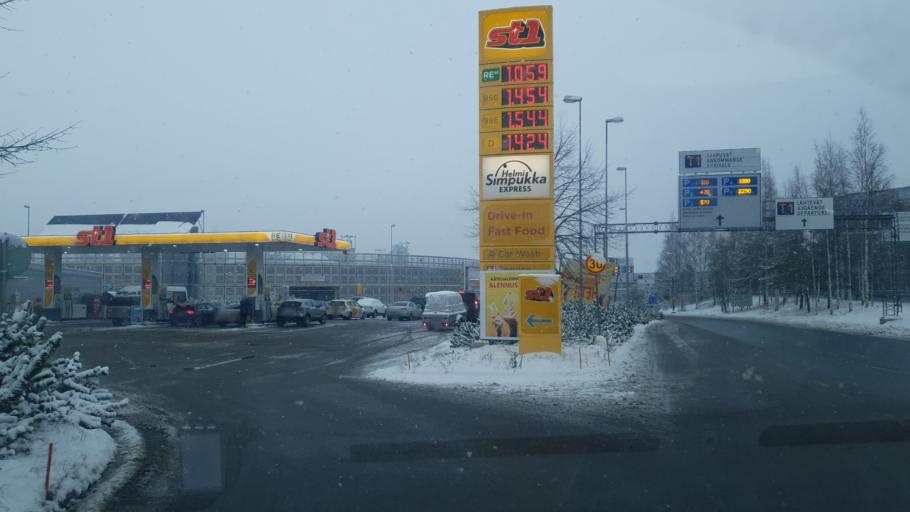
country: FI
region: Uusimaa
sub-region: Helsinki
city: Vantaa
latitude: 60.3126
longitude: 24.9715
